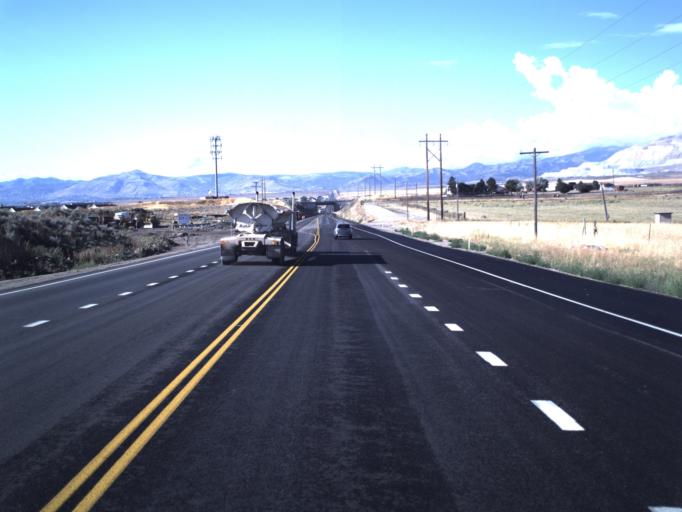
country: US
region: Utah
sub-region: Salt Lake County
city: Oquirrh
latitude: 40.6201
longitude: -112.0536
